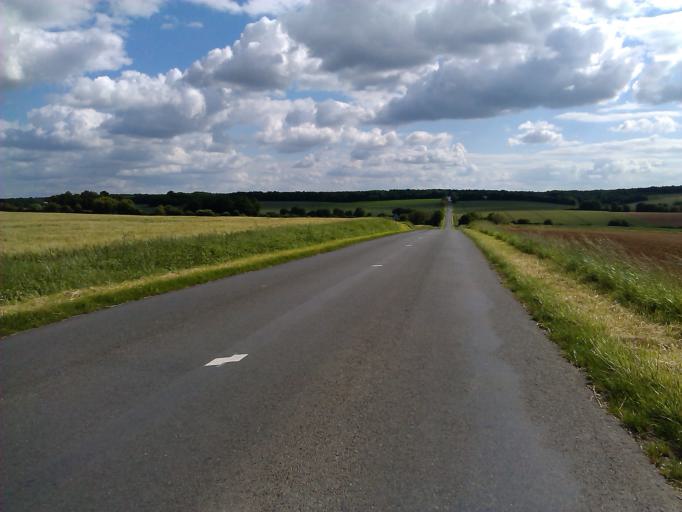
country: FR
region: Poitou-Charentes
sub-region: Departement de la Charente
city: Mansle
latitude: 45.8634
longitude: 0.1695
